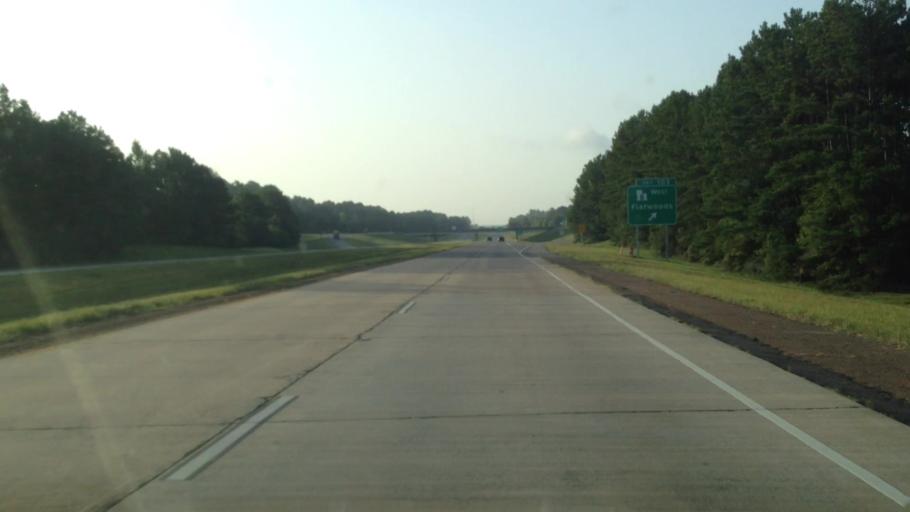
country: US
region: Louisiana
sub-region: Rapides Parish
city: Boyce
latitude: 31.4131
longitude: -92.7223
